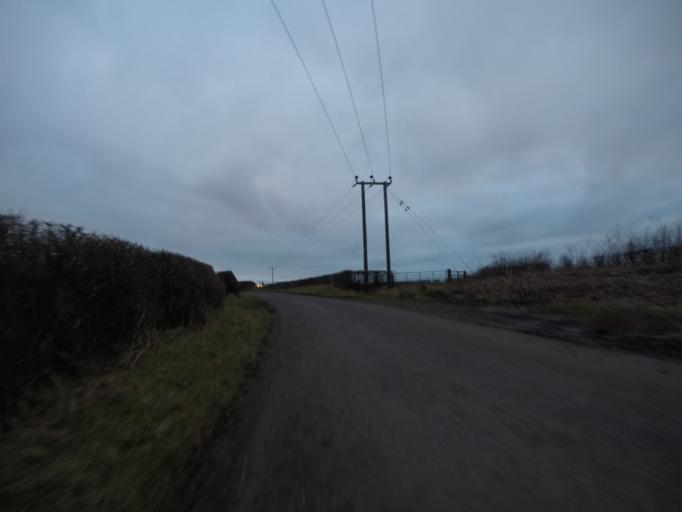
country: GB
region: Scotland
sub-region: North Ayrshire
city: Dalry
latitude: 55.6884
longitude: -4.7426
